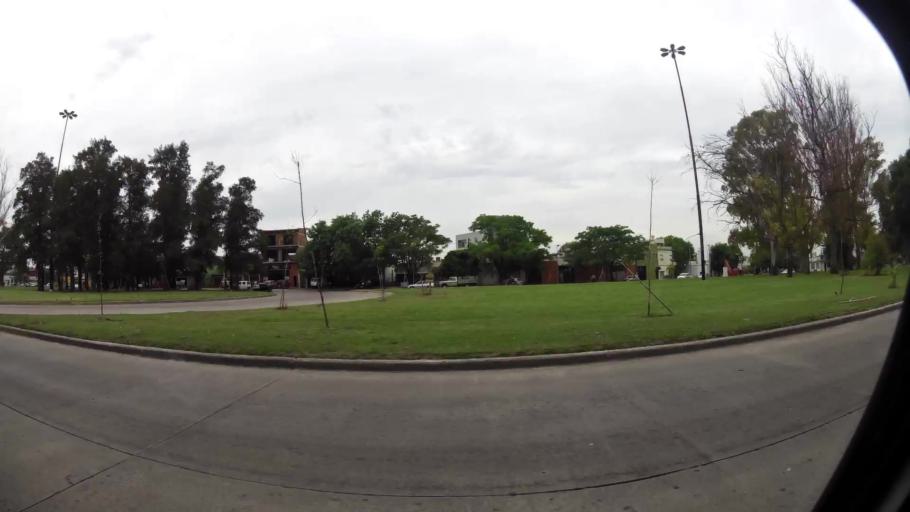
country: AR
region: Buenos Aires
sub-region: Partido de La Plata
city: La Plata
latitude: -34.9244
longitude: -57.9903
